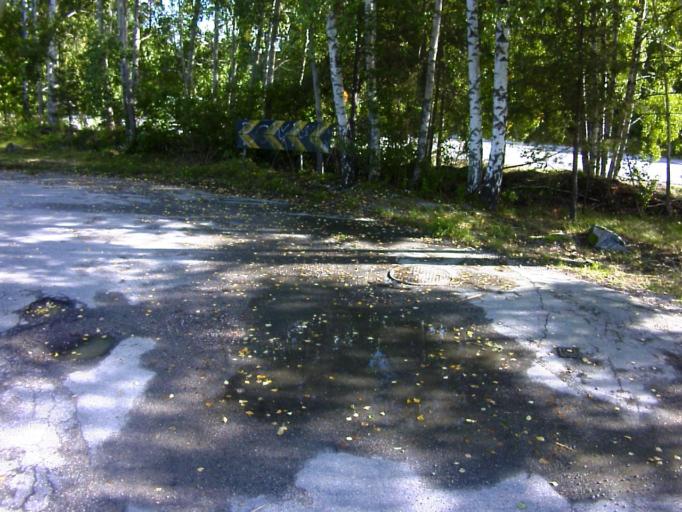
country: SE
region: Soedermanland
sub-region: Eskilstuna Kommun
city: Eskilstuna
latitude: 59.3962
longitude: 16.5450
